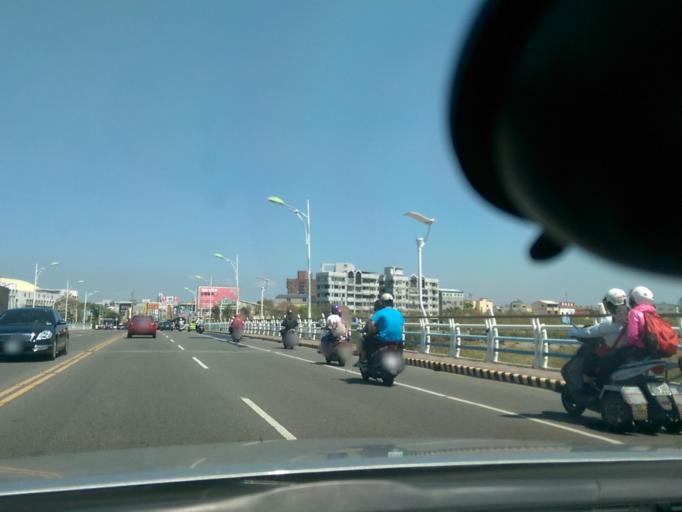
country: TW
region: Taiwan
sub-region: Chiayi
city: Jiayi Shi
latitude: 23.4581
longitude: 120.4582
